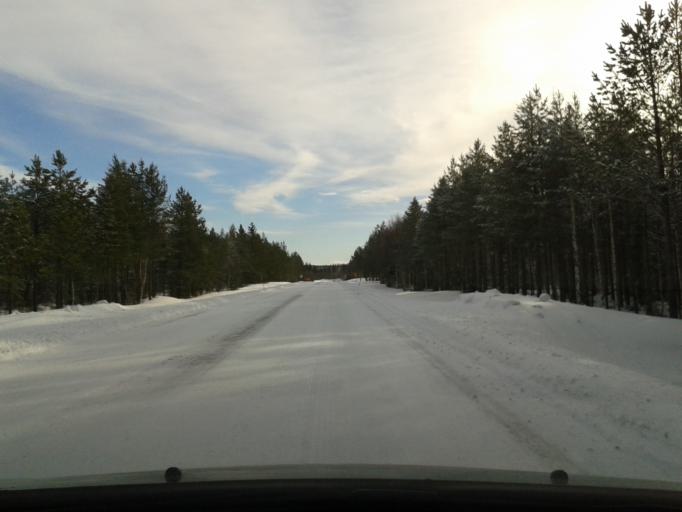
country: SE
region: Vaesterbotten
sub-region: Vilhelmina Kommun
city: Vilhelmina
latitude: 64.5288
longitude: 16.7580
